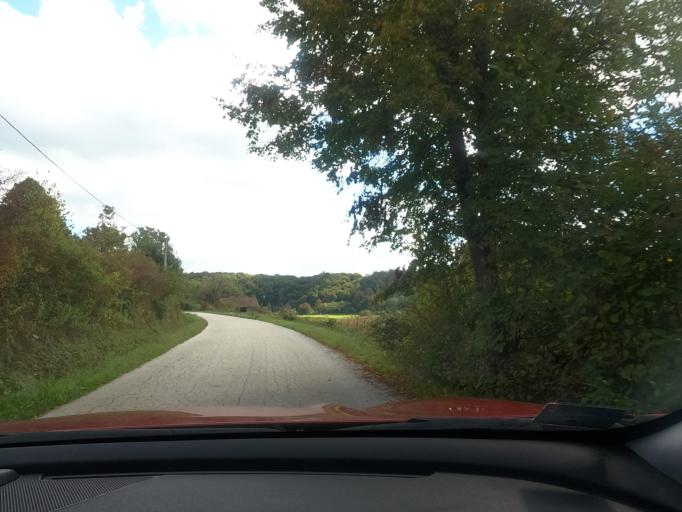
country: BA
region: Federation of Bosnia and Herzegovina
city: Velika Kladusa
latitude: 45.2130
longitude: 15.7201
